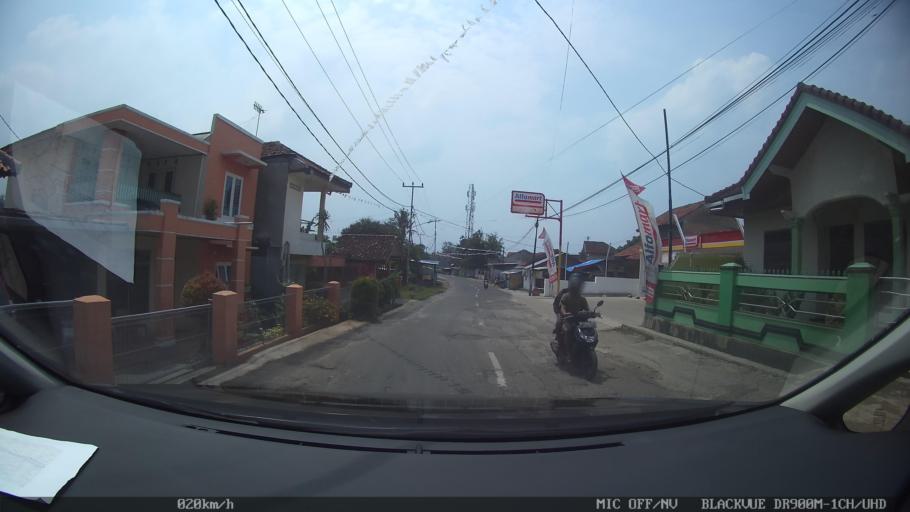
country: ID
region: Lampung
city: Bandarlampung
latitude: -5.4348
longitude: 105.2685
